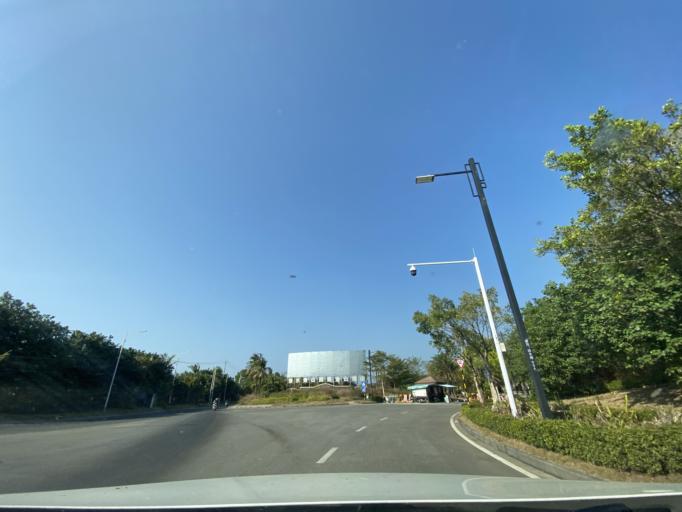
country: CN
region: Hainan
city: Yingzhou
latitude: 18.4464
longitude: 109.8461
